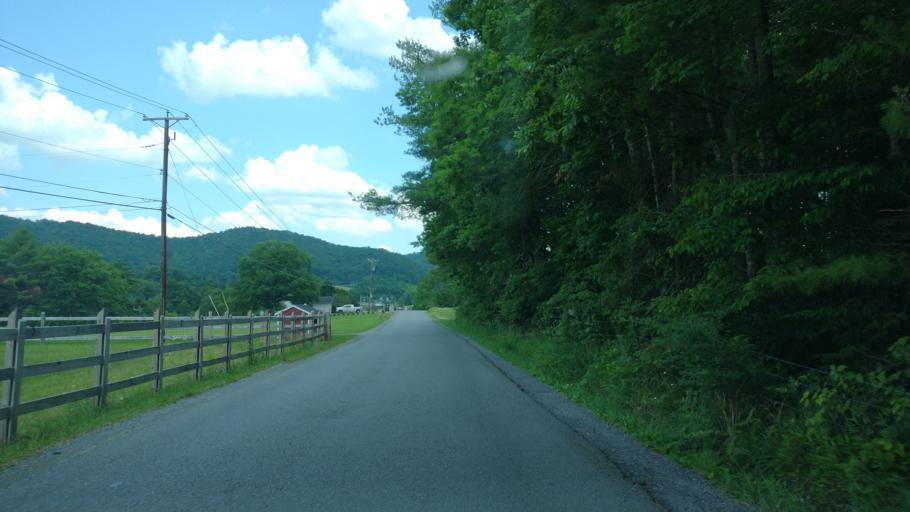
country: US
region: West Virginia
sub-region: Mercer County
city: Athens
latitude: 37.4574
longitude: -81.0160
